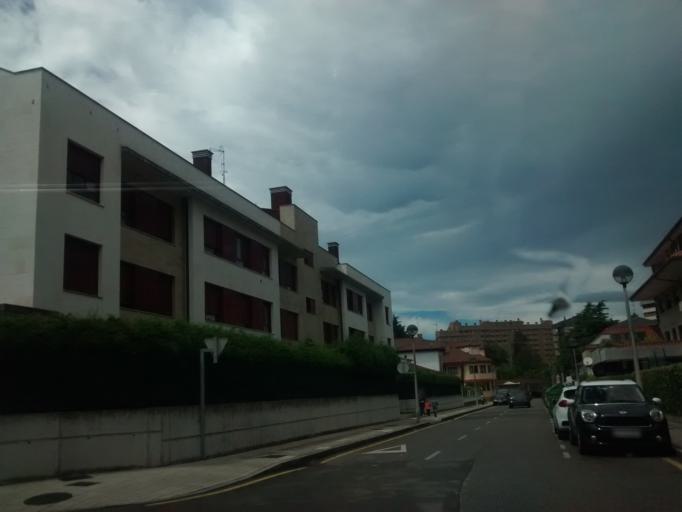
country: ES
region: Asturias
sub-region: Province of Asturias
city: Gijon
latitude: 43.5322
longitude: -5.6419
